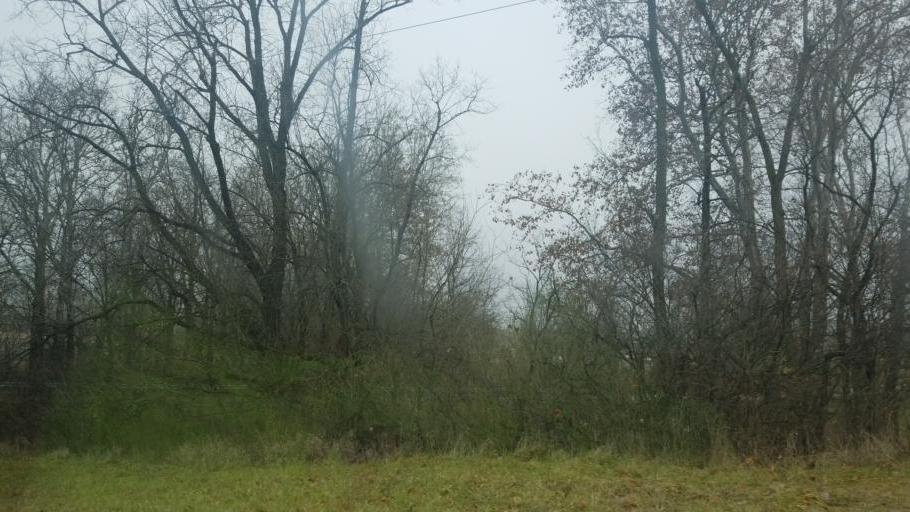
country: US
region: Ohio
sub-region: Champaign County
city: North Lewisburg
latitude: 40.2855
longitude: -83.6035
